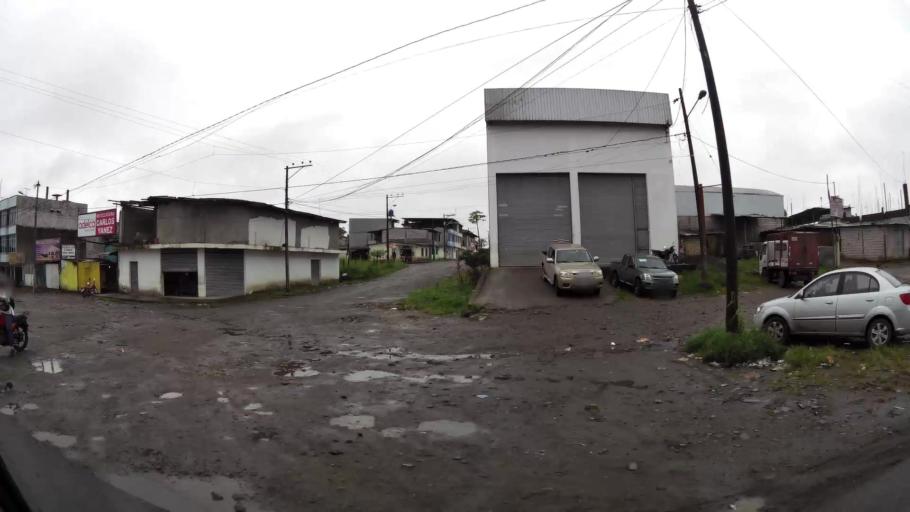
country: EC
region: Santo Domingo de los Tsachilas
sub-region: Canton Santo Domingo de los Colorados
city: Santo Domingo de los Colorados
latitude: -0.2377
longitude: -79.1756
